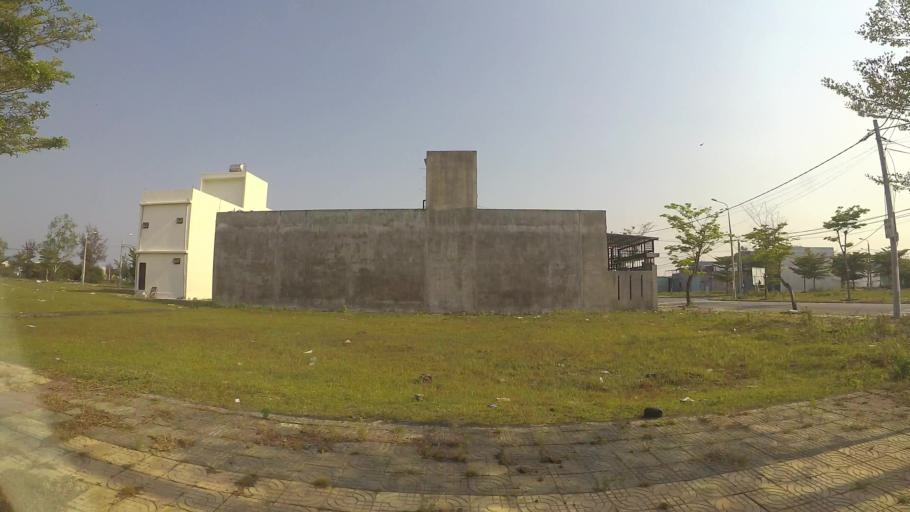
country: VN
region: Quang Nam
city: Quang Nam
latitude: 15.9489
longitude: 108.2597
